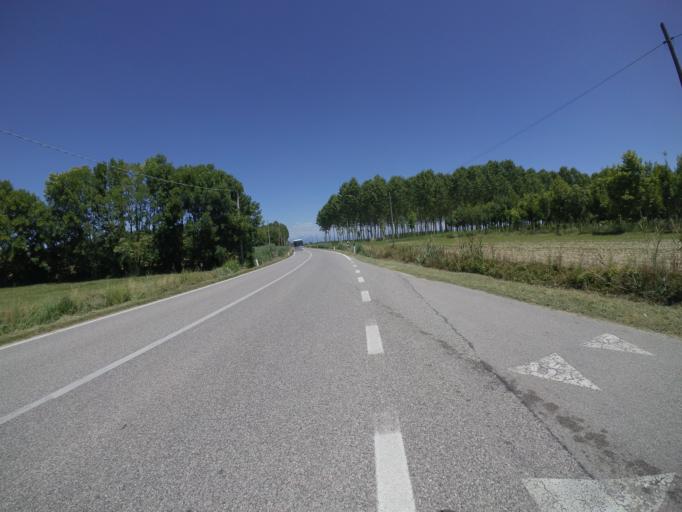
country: IT
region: Friuli Venezia Giulia
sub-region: Provincia di Udine
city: Rivignano
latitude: 45.8858
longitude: 13.0748
